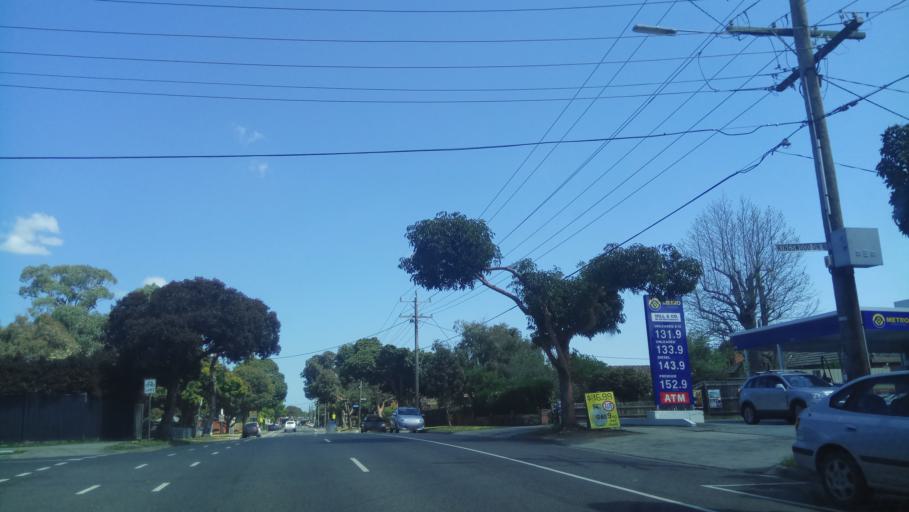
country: AU
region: Victoria
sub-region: Kingston
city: Dingley Village
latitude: -37.9808
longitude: 145.1351
